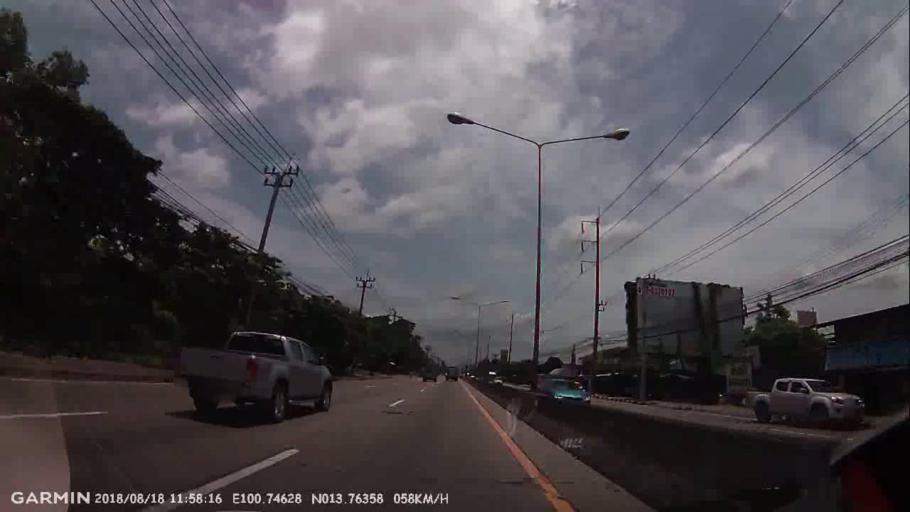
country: TH
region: Bangkok
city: Min Buri
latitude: 13.7637
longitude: 100.7463
